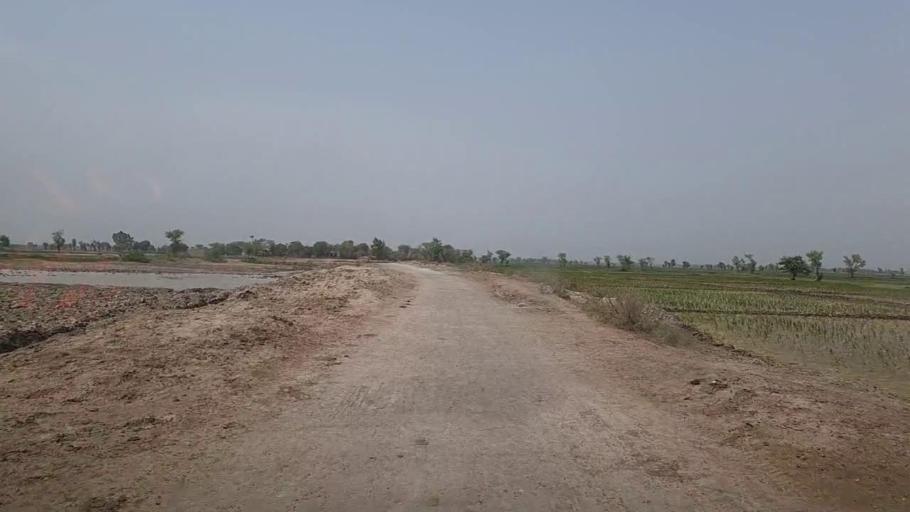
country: PK
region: Sindh
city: Sita Road
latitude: 27.0916
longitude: 67.8557
